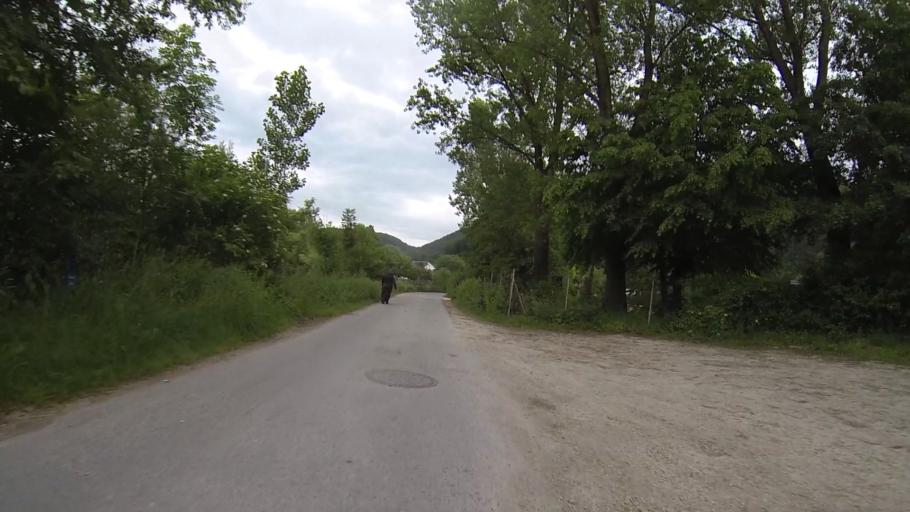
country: DE
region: Baden-Wuerttemberg
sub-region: Tuebingen Region
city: Blaubeuren
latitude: 48.4030
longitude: 9.7976
